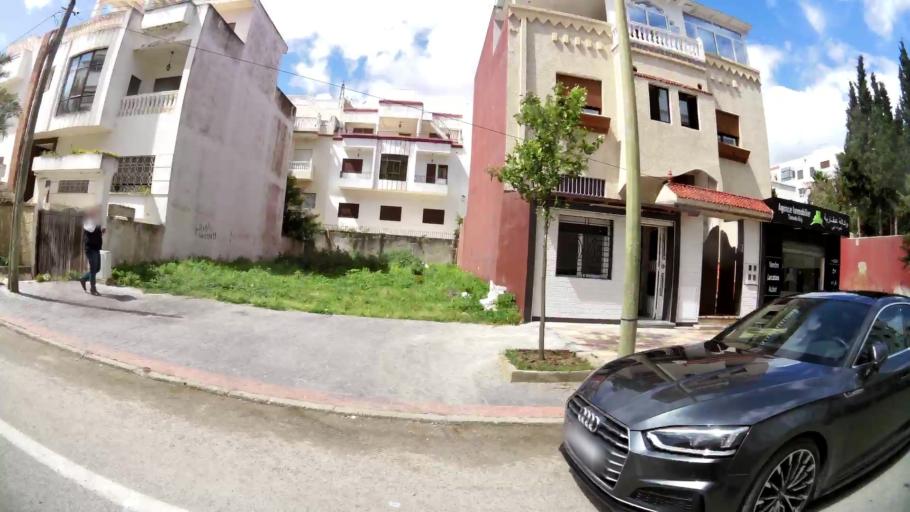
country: MA
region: Tanger-Tetouan
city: Tetouan
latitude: 35.5872
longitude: -5.3394
